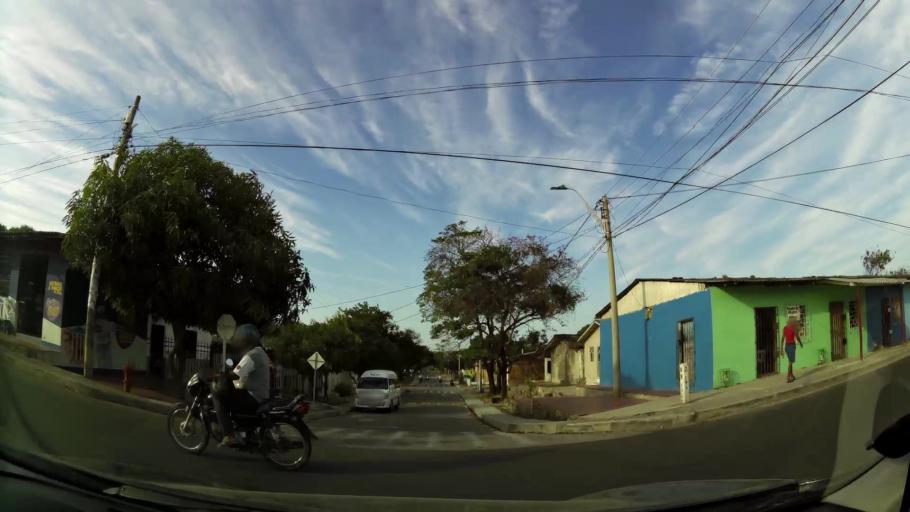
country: CO
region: Atlantico
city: Barranquilla
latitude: 10.9363
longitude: -74.8226
